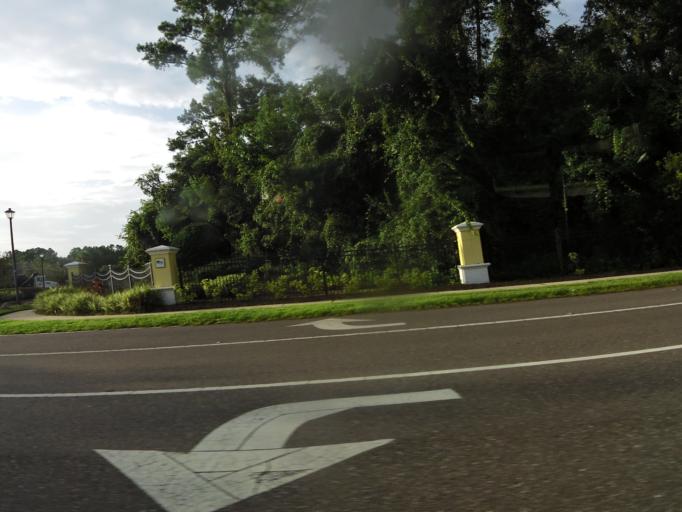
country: US
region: Florida
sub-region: Nassau County
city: Nassau Village-Ratliff
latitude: 30.4158
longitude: -81.7681
